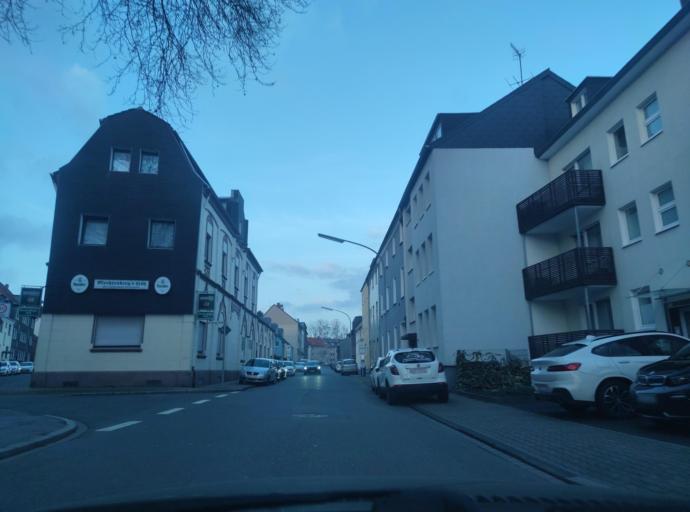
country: DE
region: North Rhine-Westphalia
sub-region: Regierungsbezirk Munster
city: Gelsenkirchen
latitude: 51.4882
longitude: 7.0897
